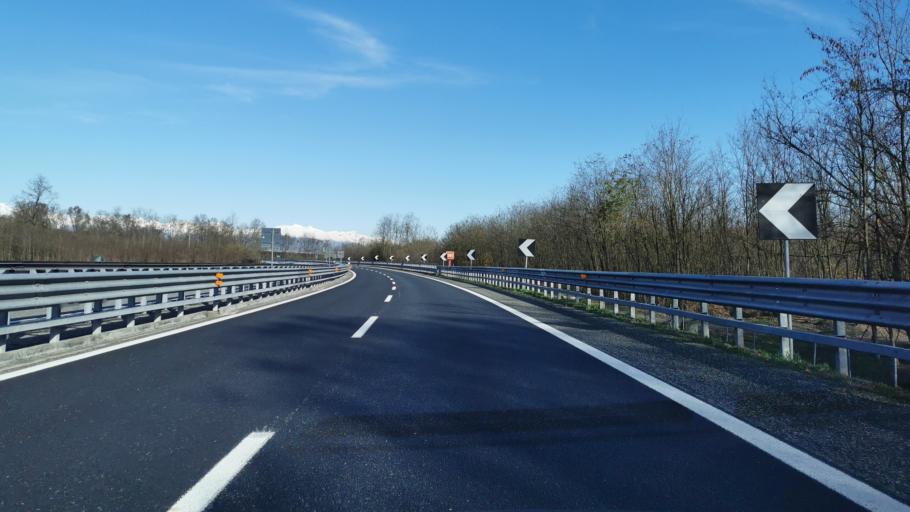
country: IT
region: Piedmont
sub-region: Provincia di Torino
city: Foglizzo
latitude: 45.2449
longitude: 7.8146
